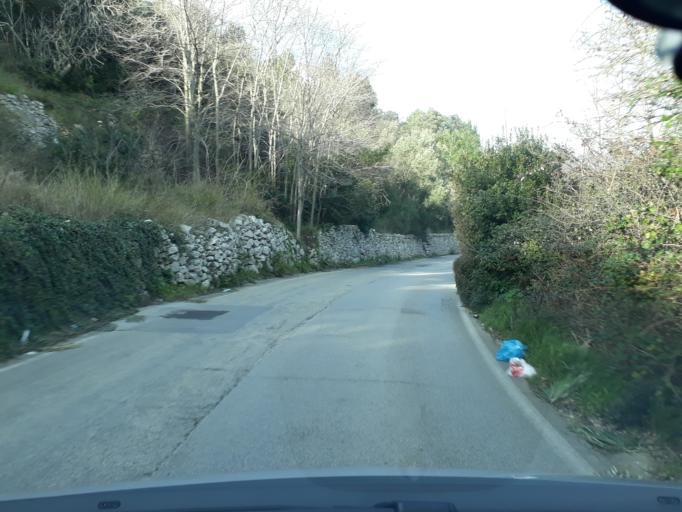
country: IT
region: Apulia
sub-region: Provincia di Brindisi
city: Lamie di Olimpie-Selva
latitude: 40.8033
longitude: 17.3522
